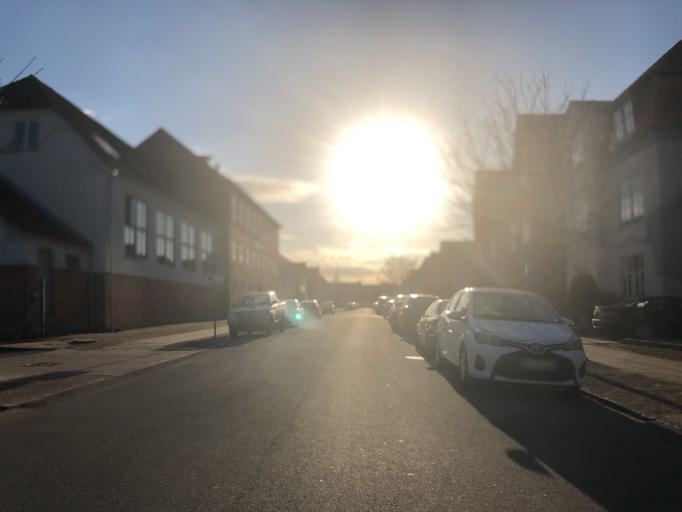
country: DK
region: Zealand
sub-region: Ringsted Kommune
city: Ringsted
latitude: 55.4479
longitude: 11.7943
